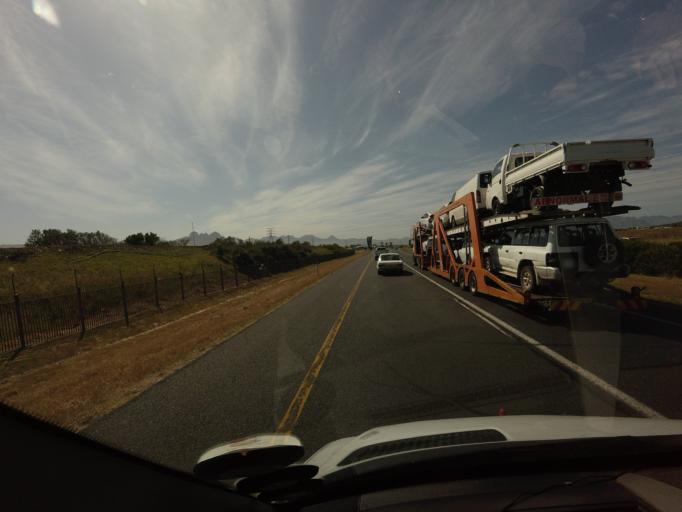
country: ZA
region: Western Cape
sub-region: Cape Winelands District Municipality
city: Stellenbosch
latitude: -34.0455
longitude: 18.7518
